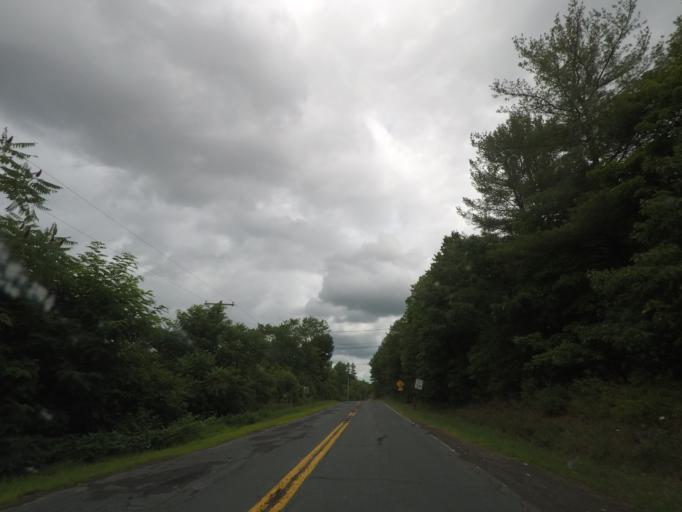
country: US
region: New York
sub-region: Rensselaer County
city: Wynantskill
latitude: 42.6773
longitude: -73.6356
